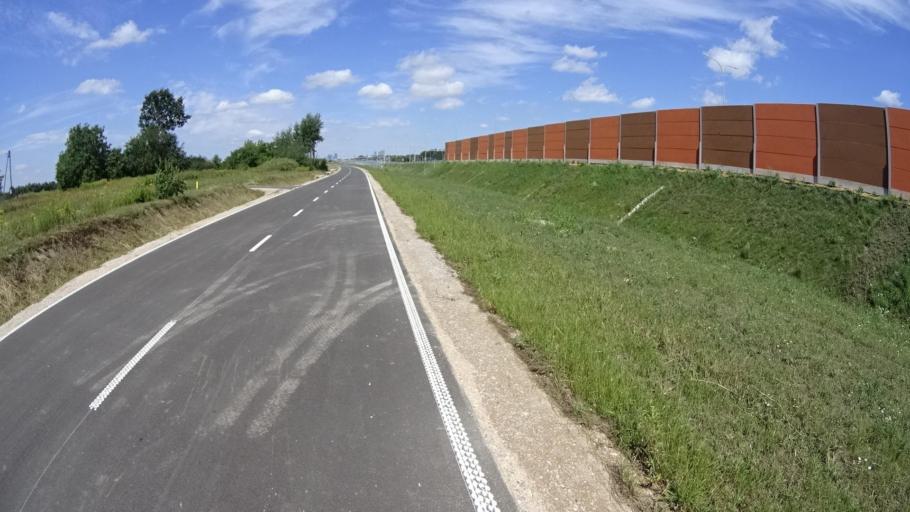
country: PL
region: Masovian Voivodeship
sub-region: Powiat piaseczynski
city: Mysiadlo
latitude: 52.1309
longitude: 20.9887
